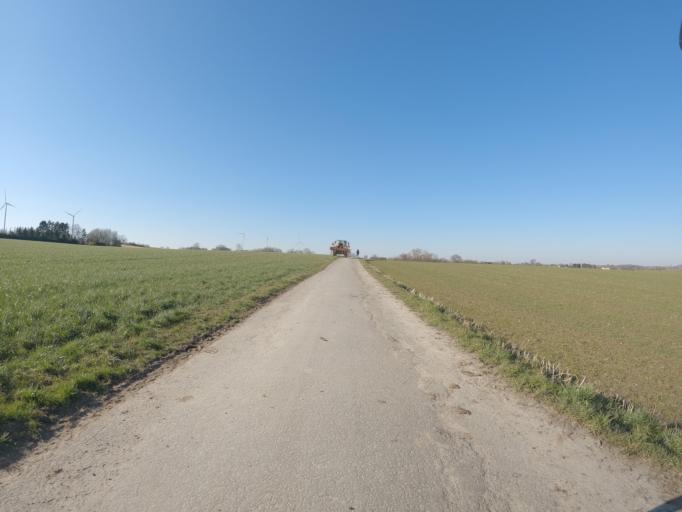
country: NL
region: Limburg
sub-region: Gemeente Kerkrade
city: Kerkrade
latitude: 50.8229
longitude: 6.0468
